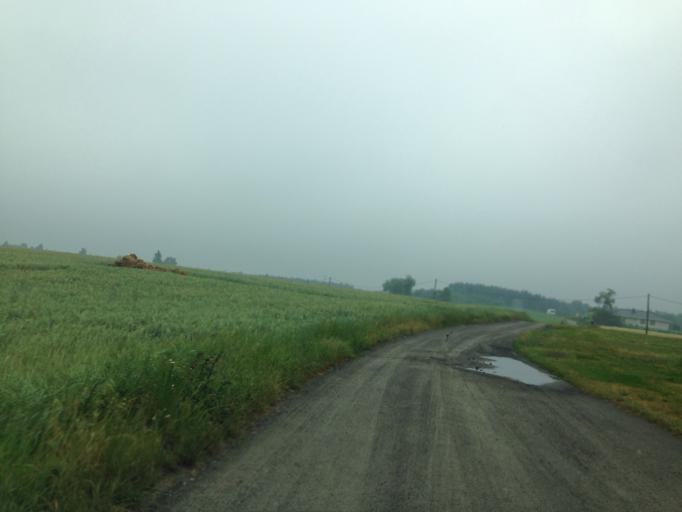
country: PL
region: Kujawsko-Pomorskie
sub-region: Powiat brodnicki
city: Brodnica
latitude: 53.3094
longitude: 19.3586
